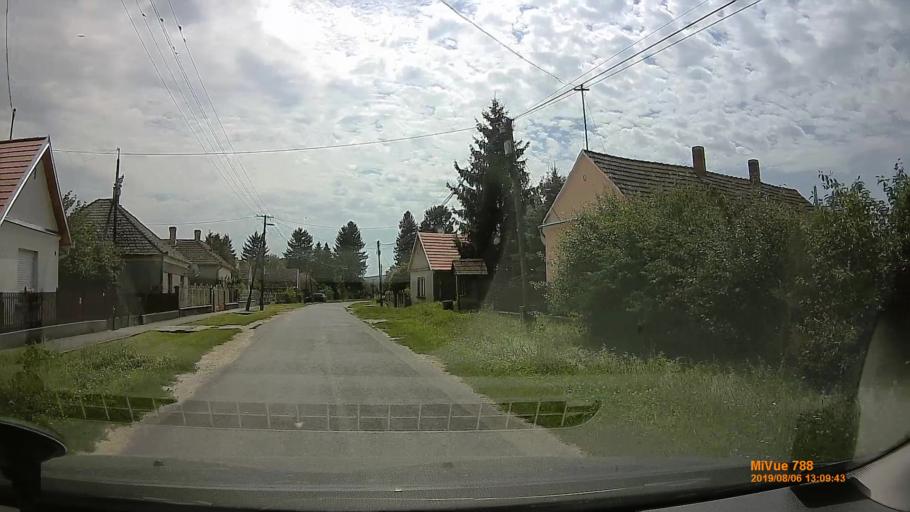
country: HU
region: Zala
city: Pacsa
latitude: 46.6219
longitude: 17.0605
